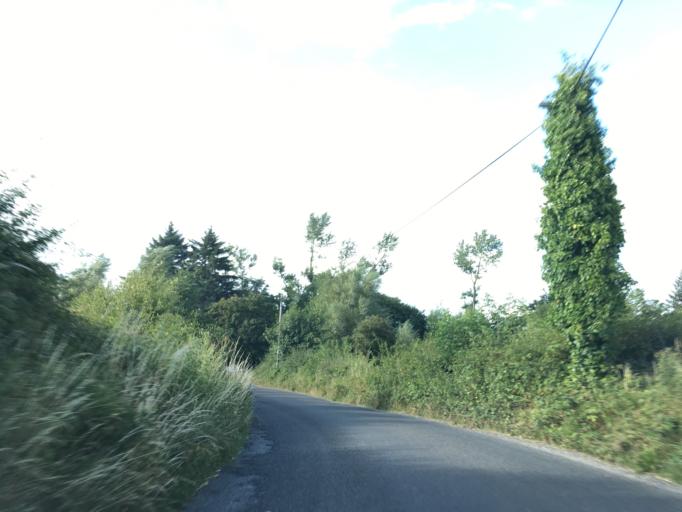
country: IE
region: Munster
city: Cahir
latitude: 52.2794
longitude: -7.9530
